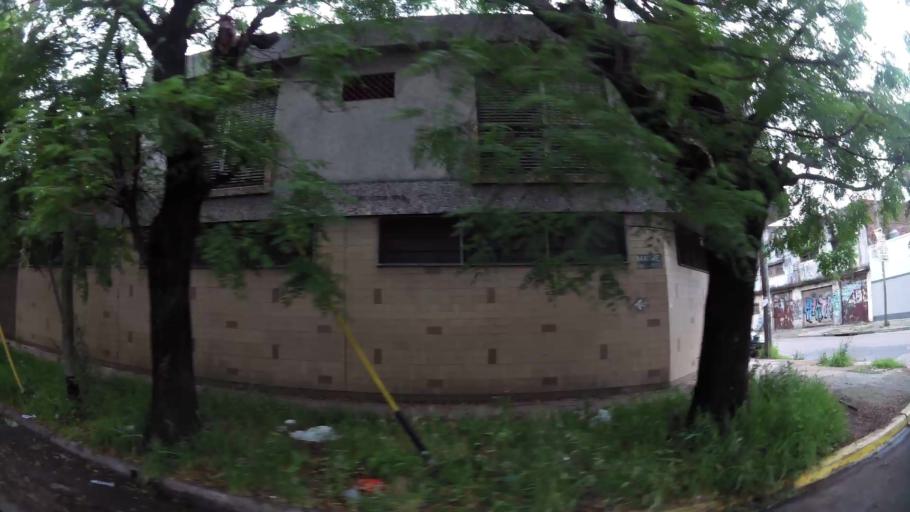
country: AR
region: Buenos Aires
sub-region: Partido de Lanus
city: Lanus
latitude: -34.6988
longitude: -58.3714
